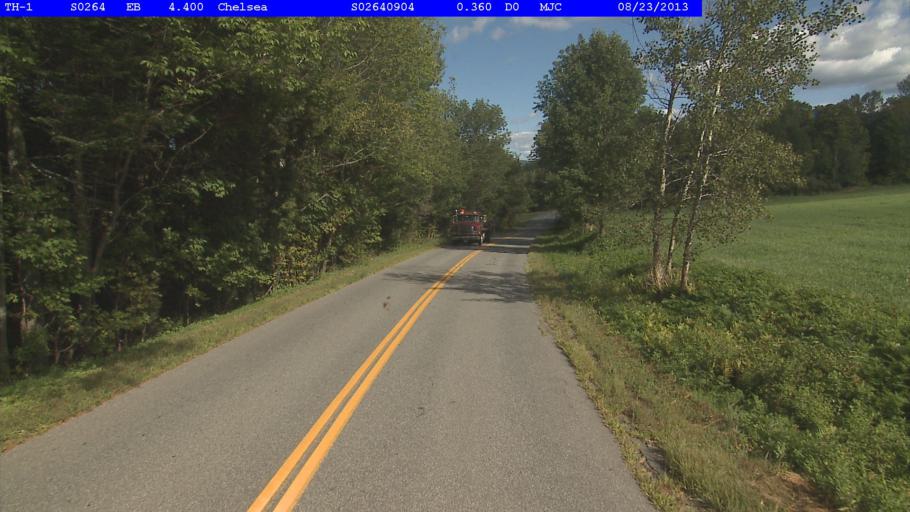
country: US
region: Vermont
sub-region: Orange County
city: Chelsea
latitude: 43.9732
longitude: -72.5053
